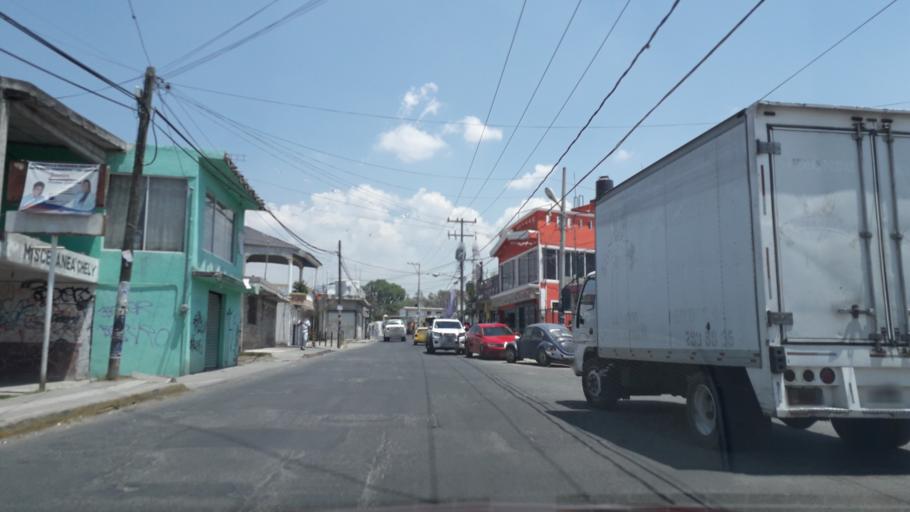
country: MX
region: Puebla
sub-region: Puebla
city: Santa Maria Xonacatepec
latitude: 19.0811
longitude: -98.1088
